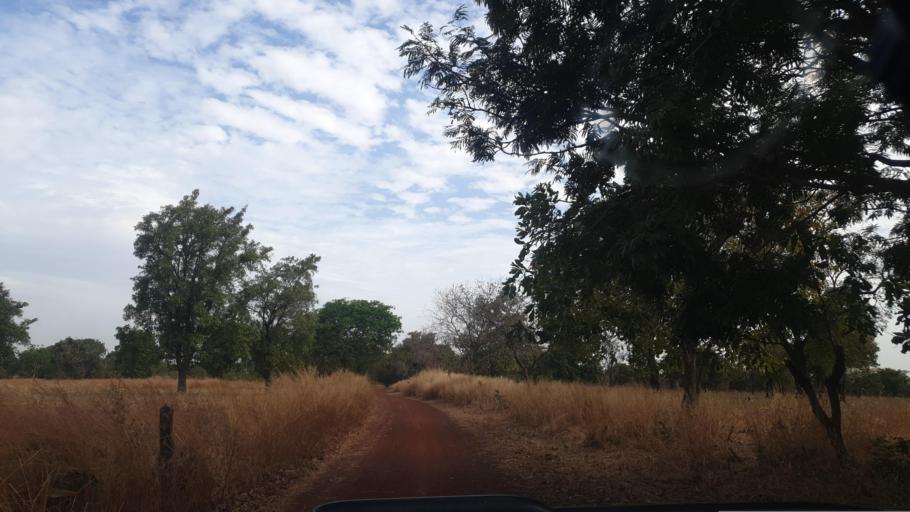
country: ML
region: Sikasso
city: Yanfolila
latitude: 11.3904
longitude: -8.0226
